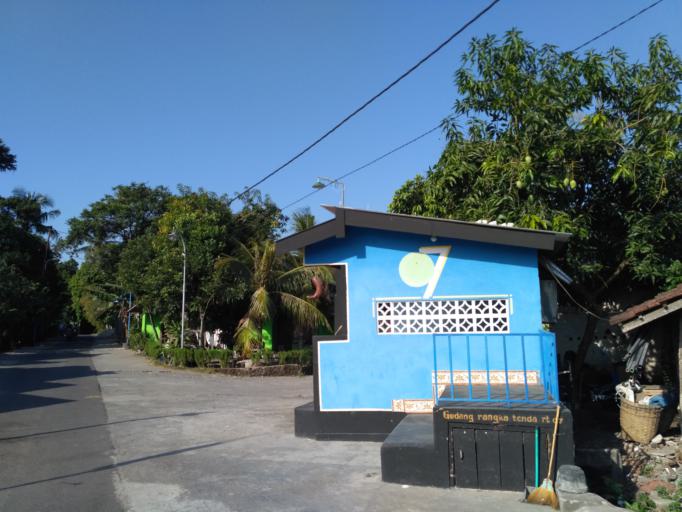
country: ID
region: Daerah Istimewa Yogyakarta
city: Depok
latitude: -7.7741
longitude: 110.4275
